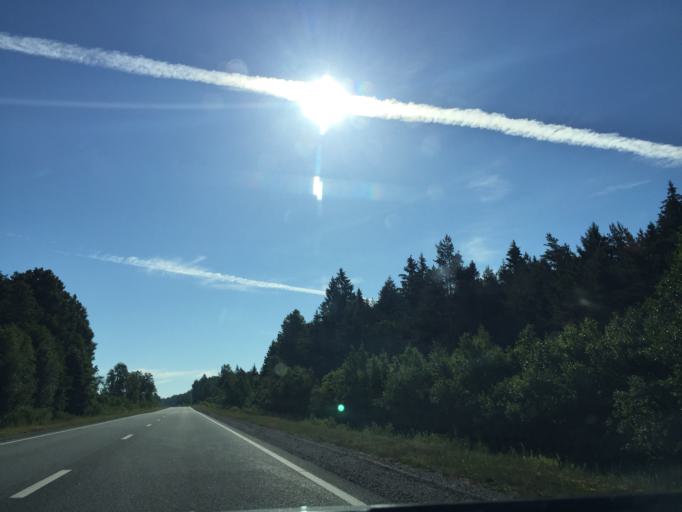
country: LV
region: Ventspils Rajons
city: Piltene
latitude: 57.3781
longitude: 21.7306
